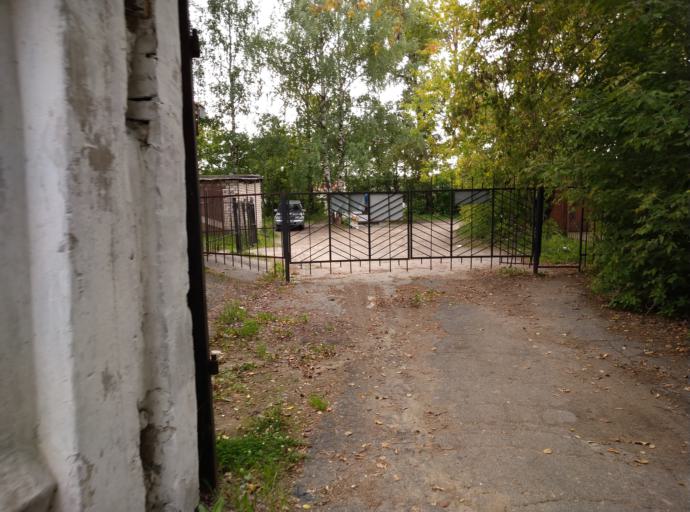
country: RU
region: Kostroma
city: Oktyabr'skiy
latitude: 57.7802
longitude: 40.9717
